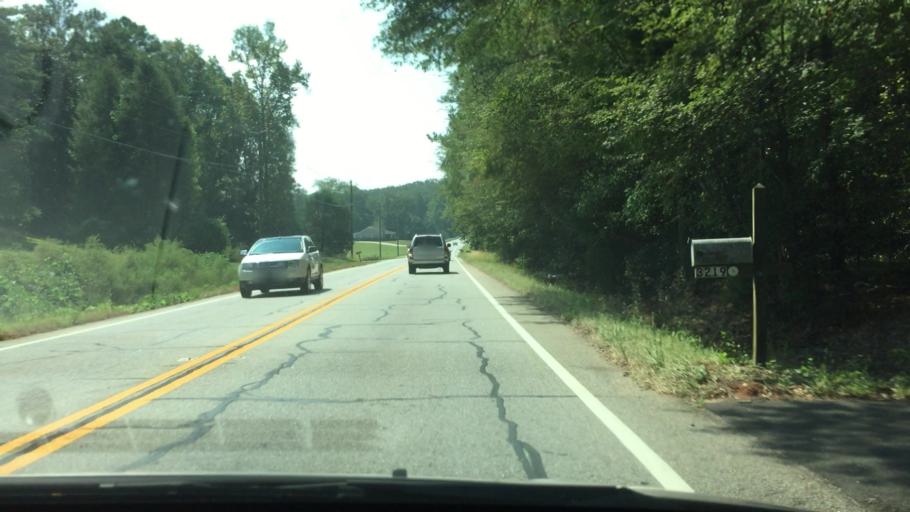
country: US
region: Georgia
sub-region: Henry County
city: McDonough
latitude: 33.5383
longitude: -84.1389
